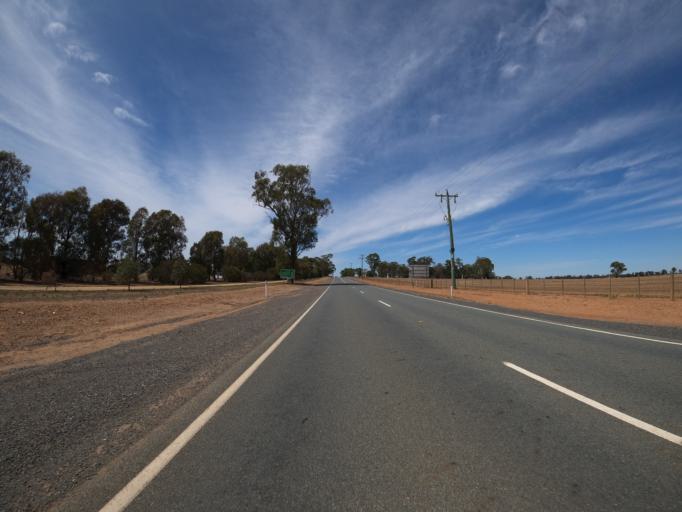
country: AU
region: Victoria
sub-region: Moira
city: Yarrawonga
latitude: -36.0423
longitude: 145.9955
